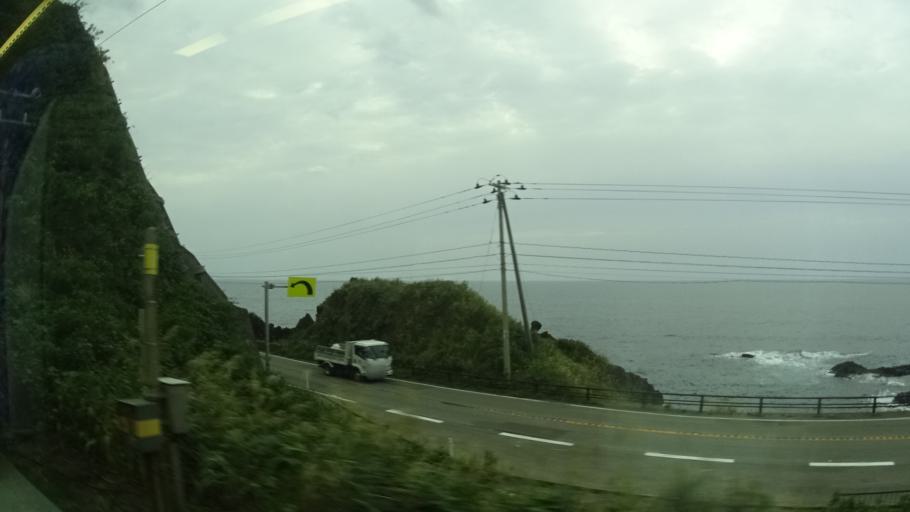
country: JP
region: Yamagata
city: Tsuruoka
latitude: 38.5967
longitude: 139.5665
